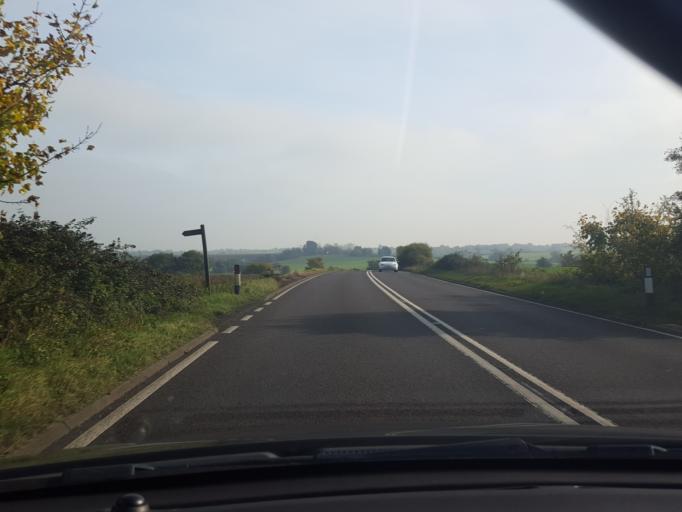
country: GB
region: England
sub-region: Suffolk
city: Shotley Gate
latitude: 51.9244
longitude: 1.1870
